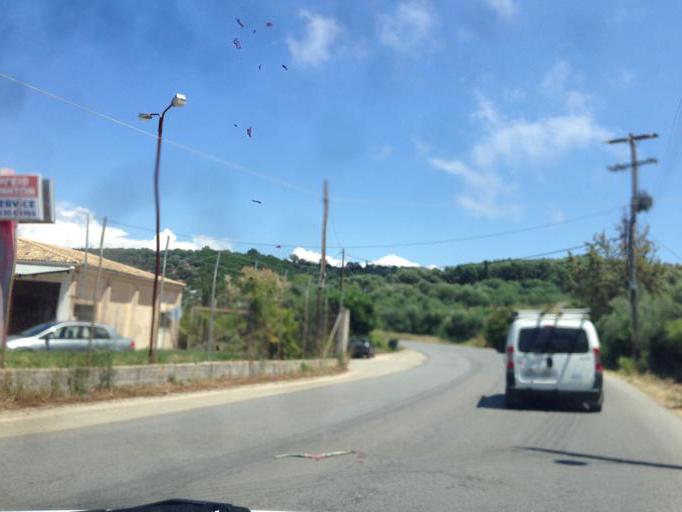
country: GR
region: Ionian Islands
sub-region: Nomos Kerkyras
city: Acharavi
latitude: 39.8059
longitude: 19.8500
